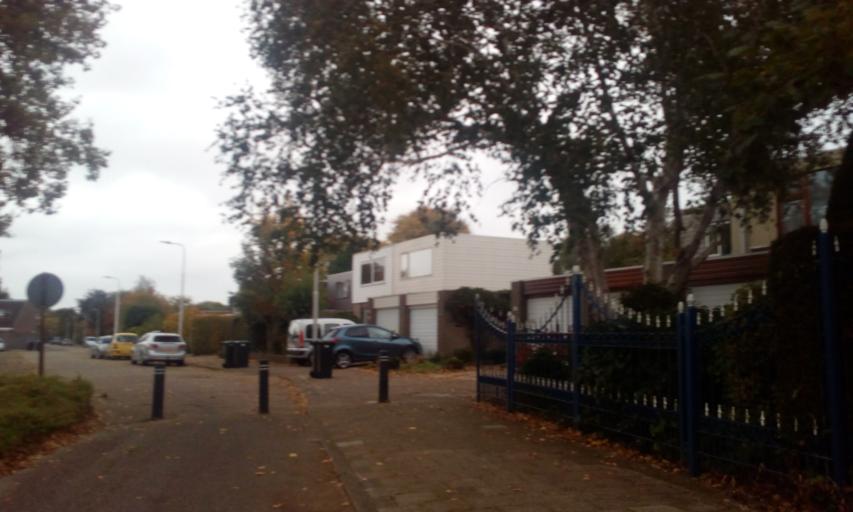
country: NL
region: South Holland
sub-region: Gemeente Lansingerland
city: Berkel en Rodenrijs
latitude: 52.0048
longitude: 4.4882
